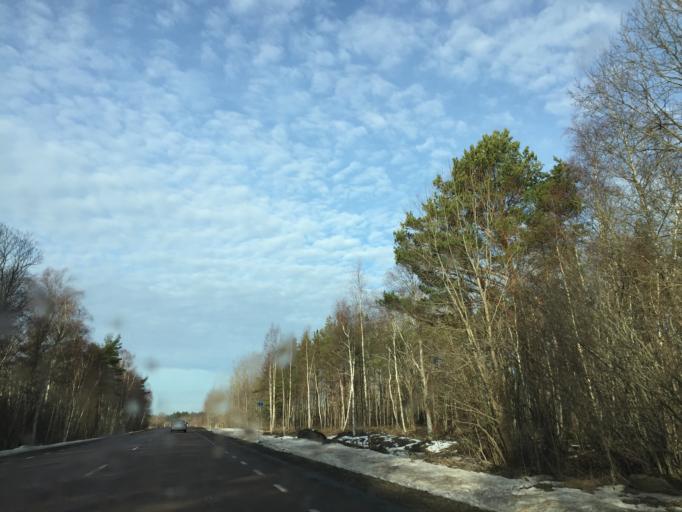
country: EE
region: Saare
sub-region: Kuressaare linn
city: Kuressaare
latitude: 58.2813
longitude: 22.4289
